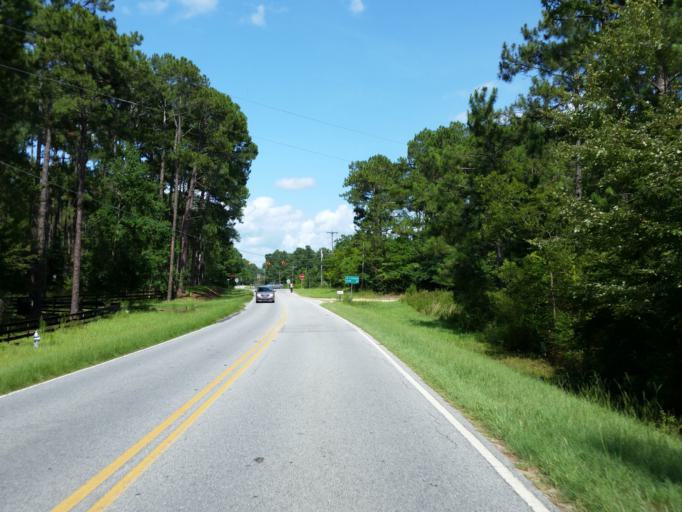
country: US
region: Georgia
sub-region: Tift County
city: Tifton
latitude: 31.5049
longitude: -83.5026
